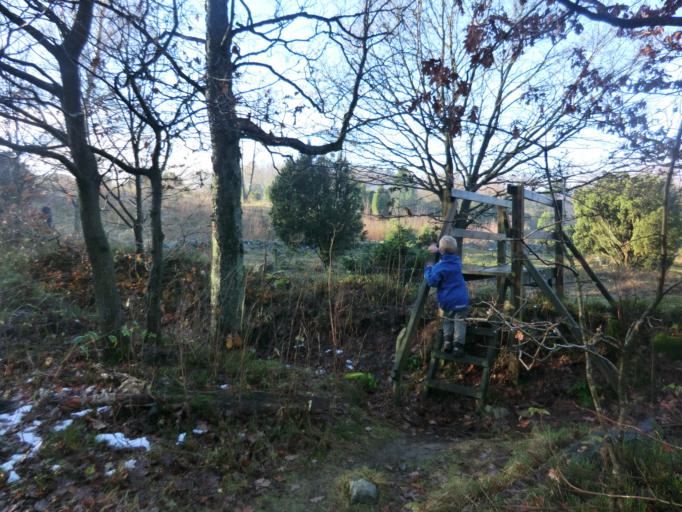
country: SE
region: Skane
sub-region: Lunds Kommun
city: Genarp
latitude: 55.6971
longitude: 13.3659
